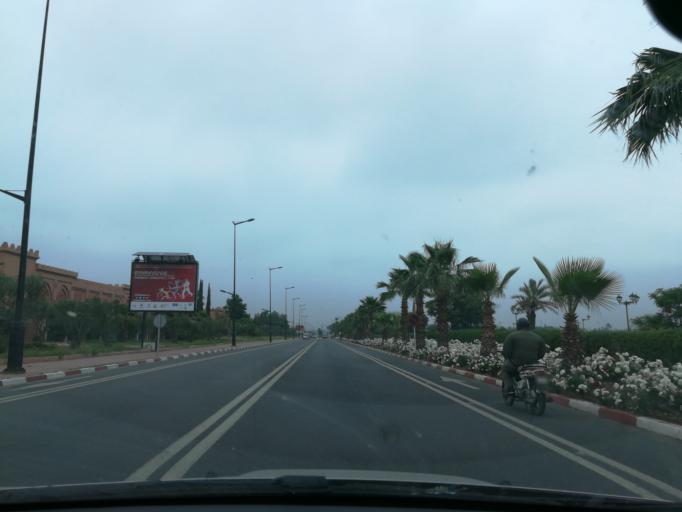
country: MA
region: Marrakech-Tensift-Al Haouz
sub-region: Marrakech
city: Marrakesh
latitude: 31.5981
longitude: -7.9869
